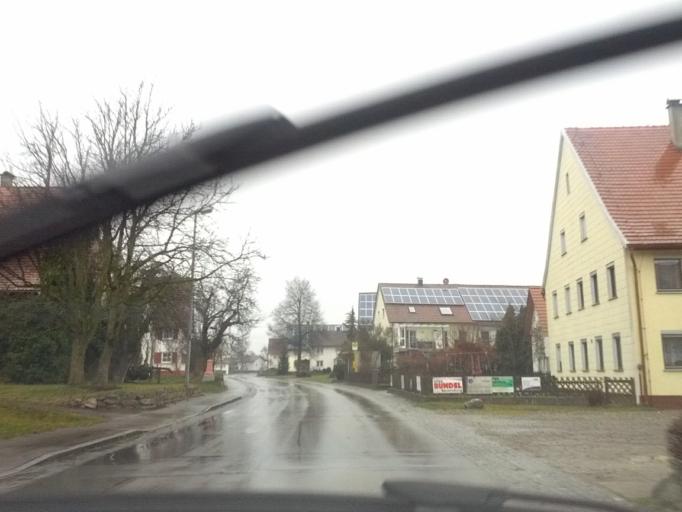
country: DE
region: Baden-Wuerttemberg
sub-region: Tuebingen Region
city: Erlenmoos
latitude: 48.0534
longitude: 9.9780
